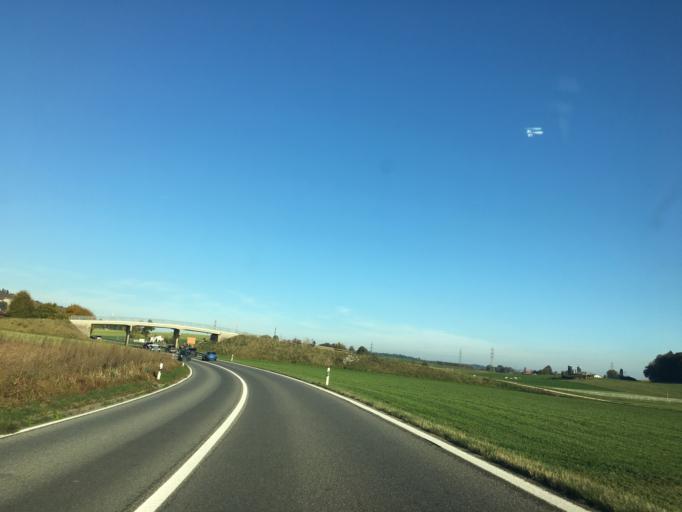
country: CH
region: Bern
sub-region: Oberaargau
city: Attiswil
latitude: 47.2439
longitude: 7.6137
